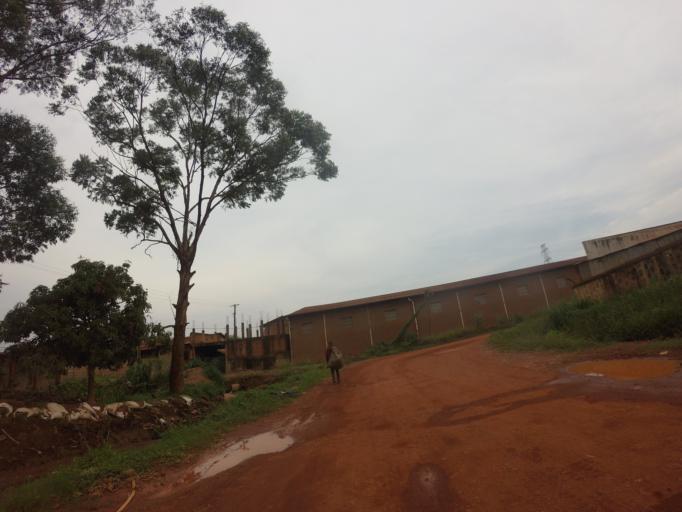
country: UG
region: Central Region
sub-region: Wakiso District
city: Kireka
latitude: 0.3389
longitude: 32.6230
